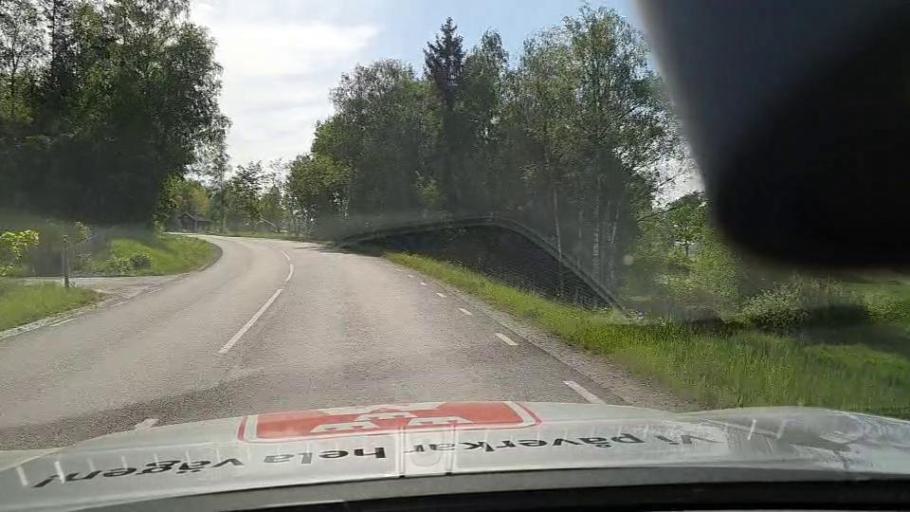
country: SE
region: Soedermanland
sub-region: Eskilstuna Kommun
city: Eskilstuna
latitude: 59.3182
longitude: 16.5715
